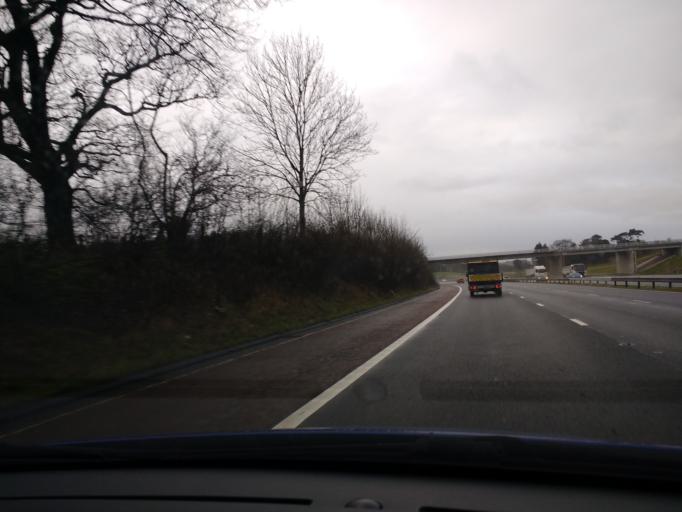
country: GB
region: England
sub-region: Lancashire
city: Bolton le Sands
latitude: 54.0812
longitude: -2.7696
